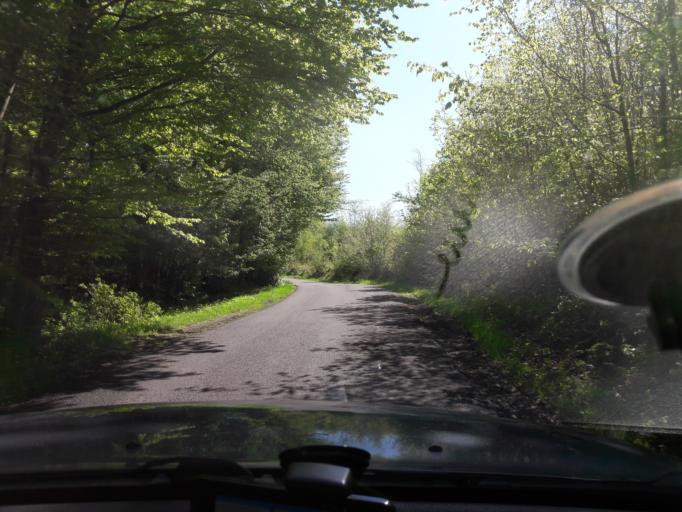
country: SK
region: Banskobystricky
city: Svaety Anton
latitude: 48.4003
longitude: 18.9546
